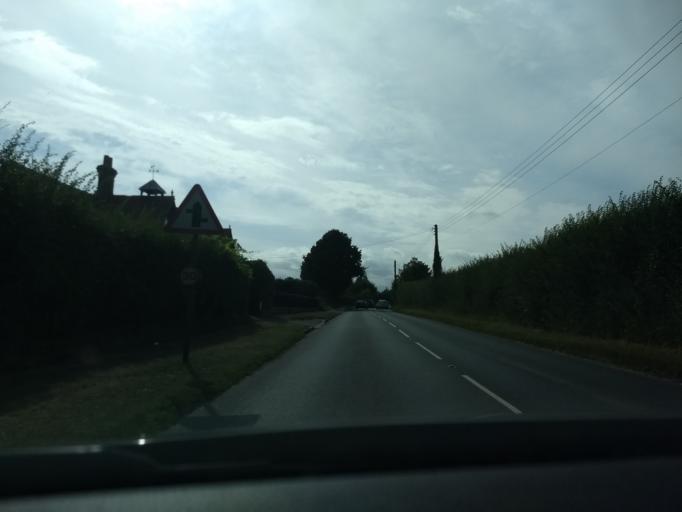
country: GB
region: England
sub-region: Suffolk
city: Ipswich
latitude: 52.0026
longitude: 1.1795
